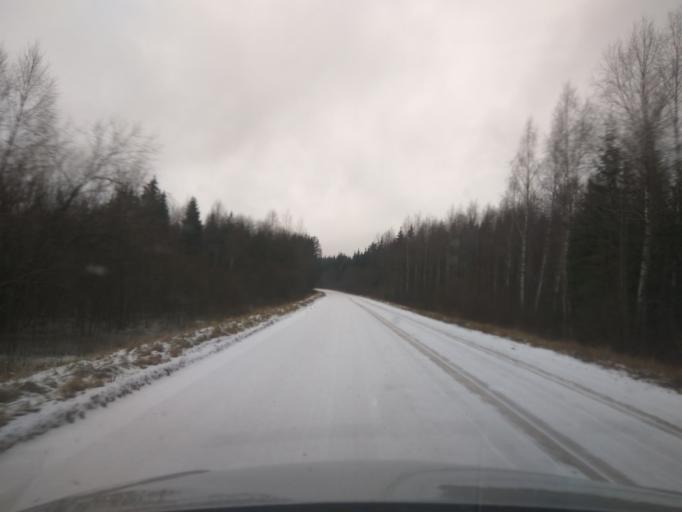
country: LV
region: Saldus Rajons
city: Saldus
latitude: 56.8159
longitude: 22.3347
